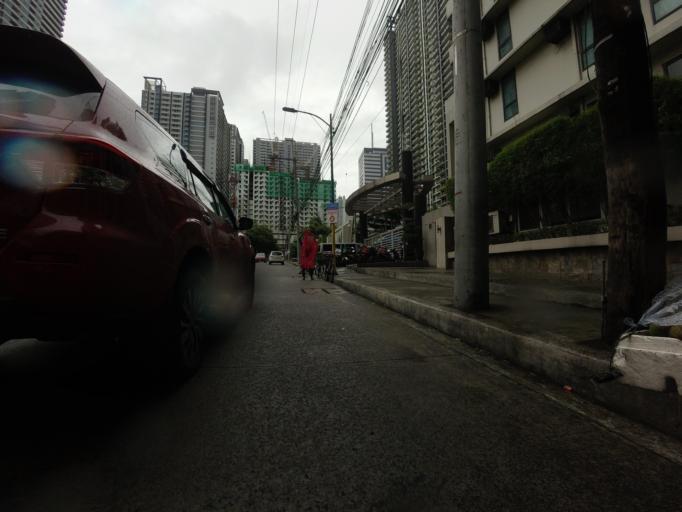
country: PH
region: Metro Manila
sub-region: Mandaluyong
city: Mandaluyong City
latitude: 14.5748
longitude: 121.0507
